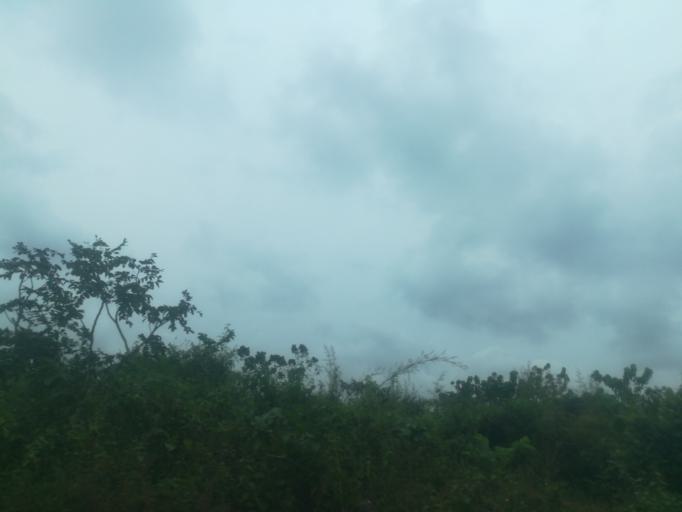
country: NG
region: Ogun
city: Ayetoro
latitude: 7.1052
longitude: 3.1432
